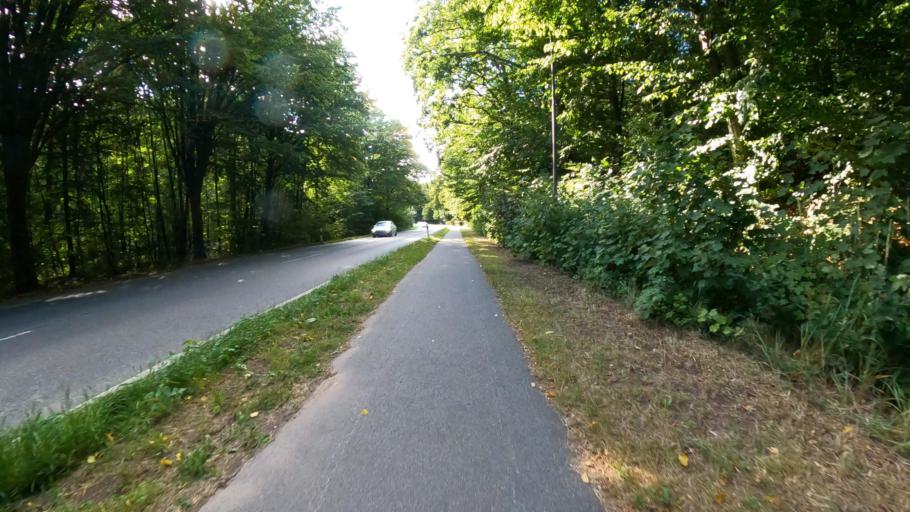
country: DE
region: Schleswig-Holstein
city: Grosshansdorf
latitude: 53.6637
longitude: 10.2656
